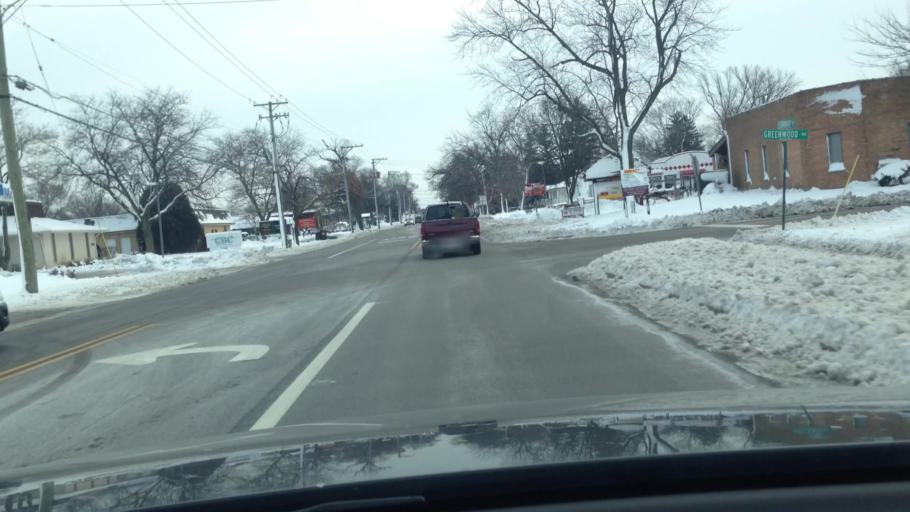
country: US
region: Illinois
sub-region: McHenry County
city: Woodstock
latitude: 42.3276
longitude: -88.4432
